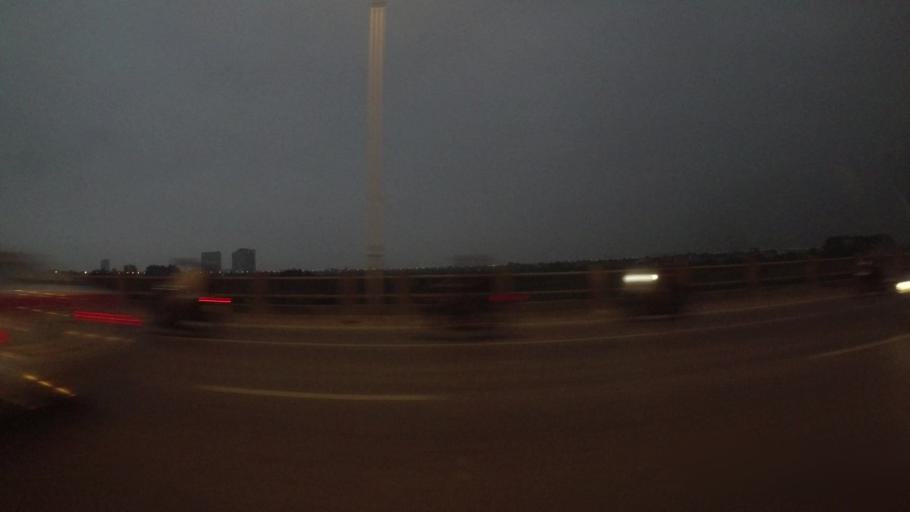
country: VN
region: Ha Noi
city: Hoan Kiem
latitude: 21.0202
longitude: 105.8921
